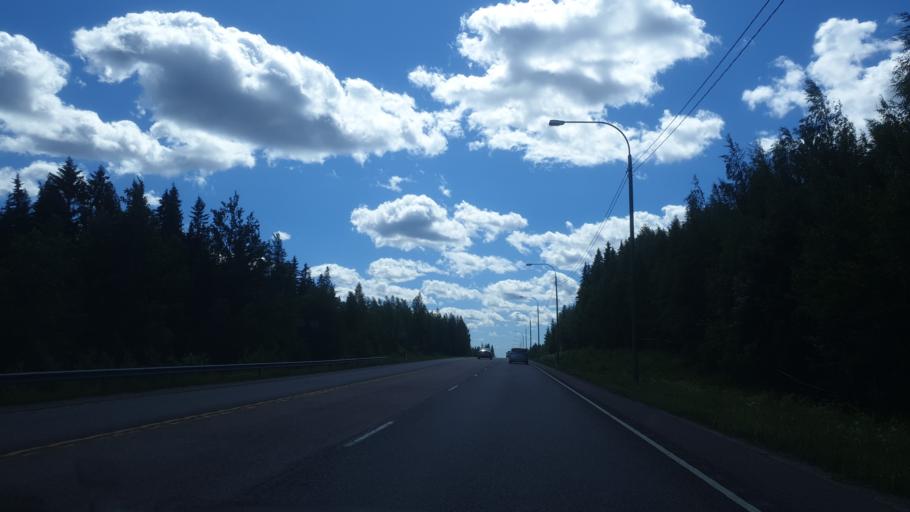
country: FI
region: Northern Savo
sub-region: Varkaus
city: Varkaus
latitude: 62.3822
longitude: 27.8093
